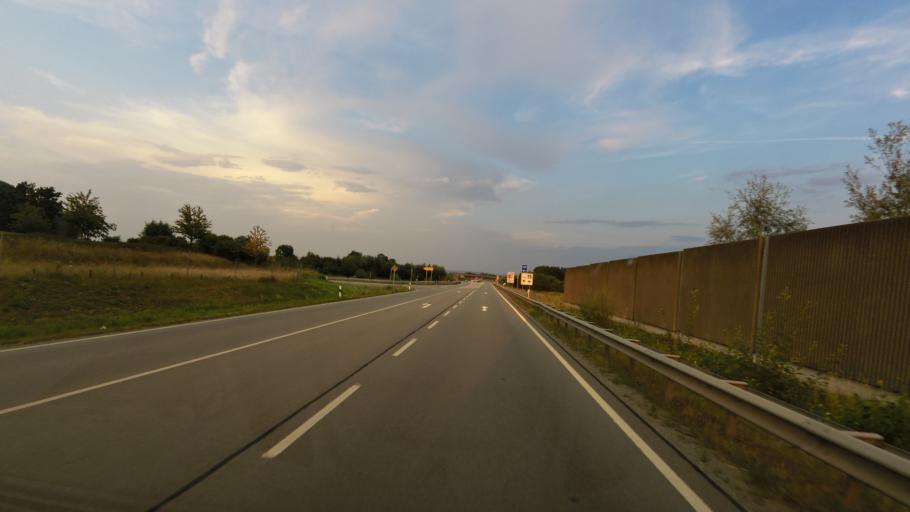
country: DE
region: Bavaria
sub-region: Lower Bavaria
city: Ering
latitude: 48.3078
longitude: 13.1675
